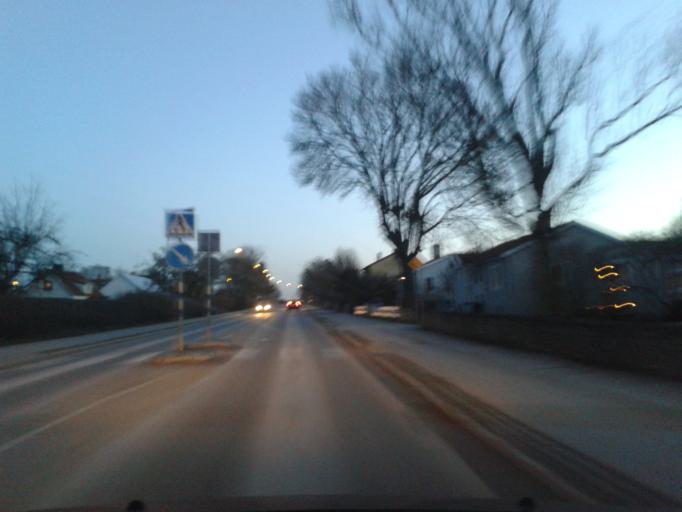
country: SE
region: Gotland
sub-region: Gotland
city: Visby
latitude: 57.6304
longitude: 18.3144
